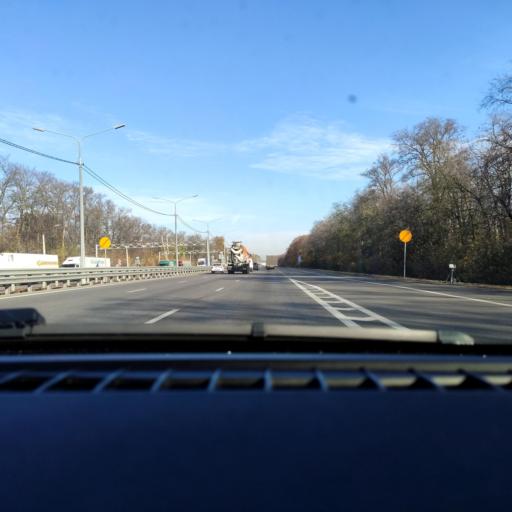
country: RU
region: Voronezj
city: Podgornoye
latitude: 51.8067
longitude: 39.2048
